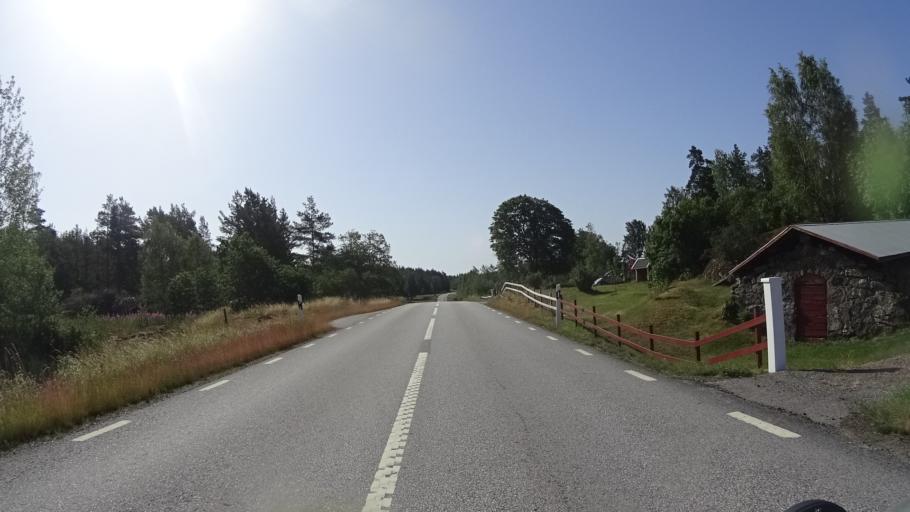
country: SE
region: OEstergoetland
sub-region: Atvidabergs Kommun
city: Atvidaberg
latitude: 58.0857
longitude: 16.1440
